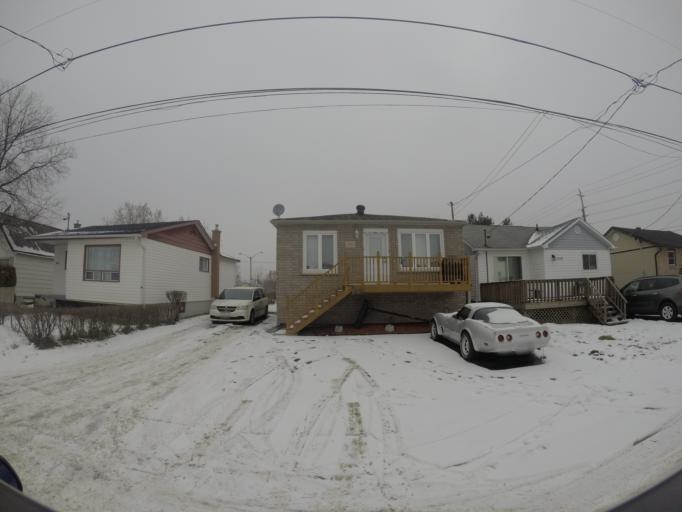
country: CA
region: Ontario
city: Greater Sudbury
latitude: 46.5060
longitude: -80.9809
